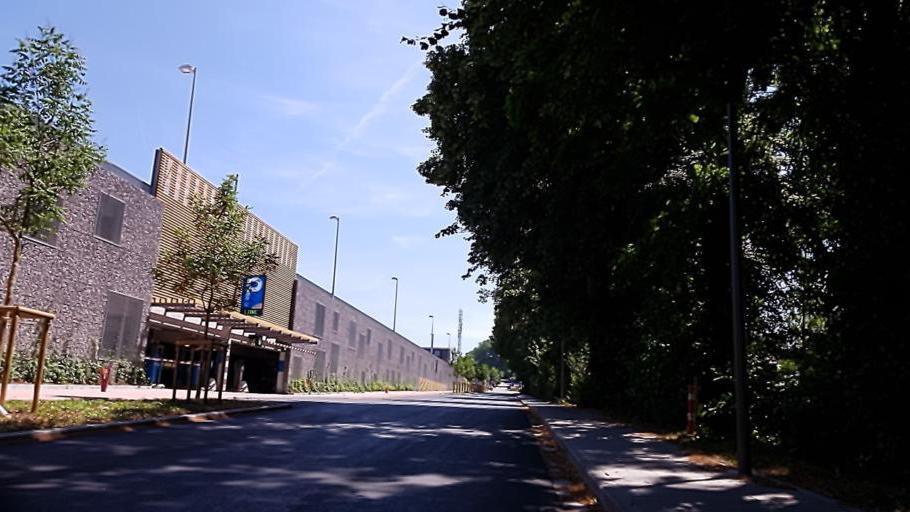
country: BE
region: Wallonia
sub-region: Province du Brabant Wallon
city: La Hulpe
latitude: 50.7396
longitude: 4.4948
